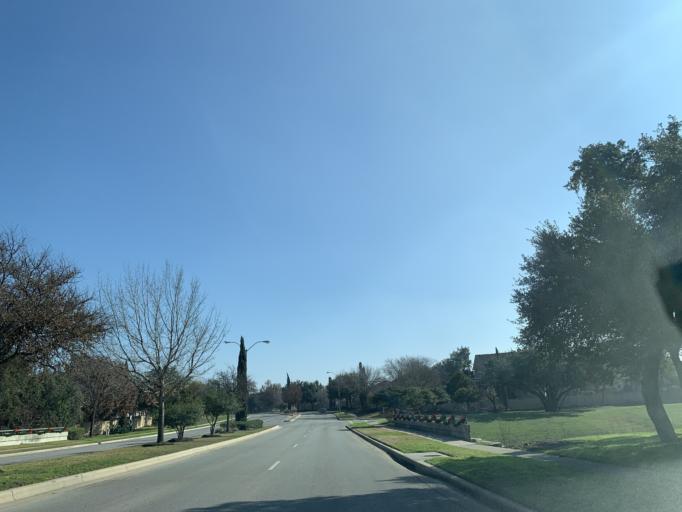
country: US
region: Texas
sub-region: Williamson County
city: Round Rock
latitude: 30.5082
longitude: -97.6280
